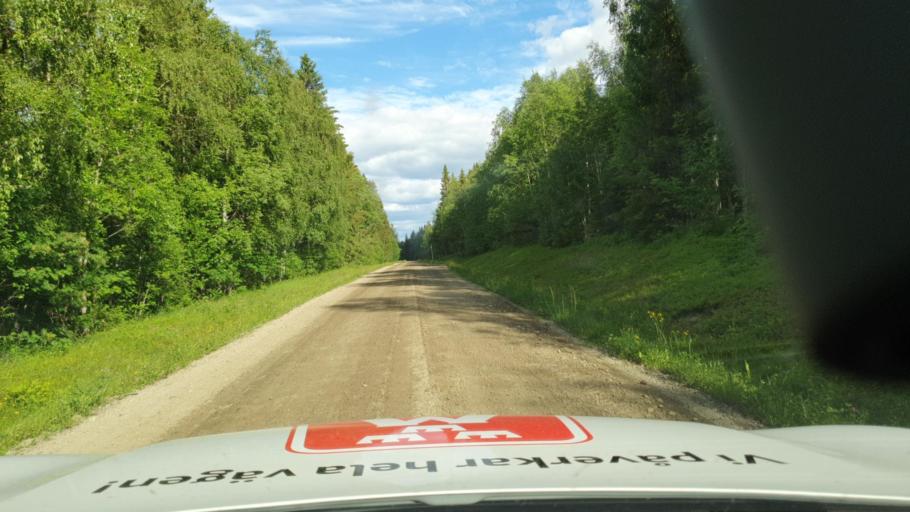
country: SE
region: Vaesterbotten
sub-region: Lycksele Kommun
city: Lycksele
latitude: 64.3223
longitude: 18.3317
